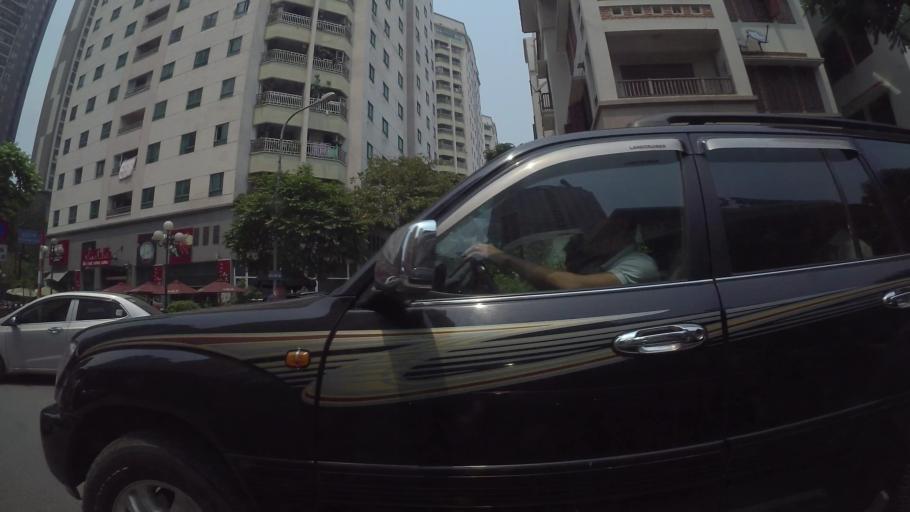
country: VN
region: Ha Noi
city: Thanh Xuan
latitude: 21.0089
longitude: 105.8020
